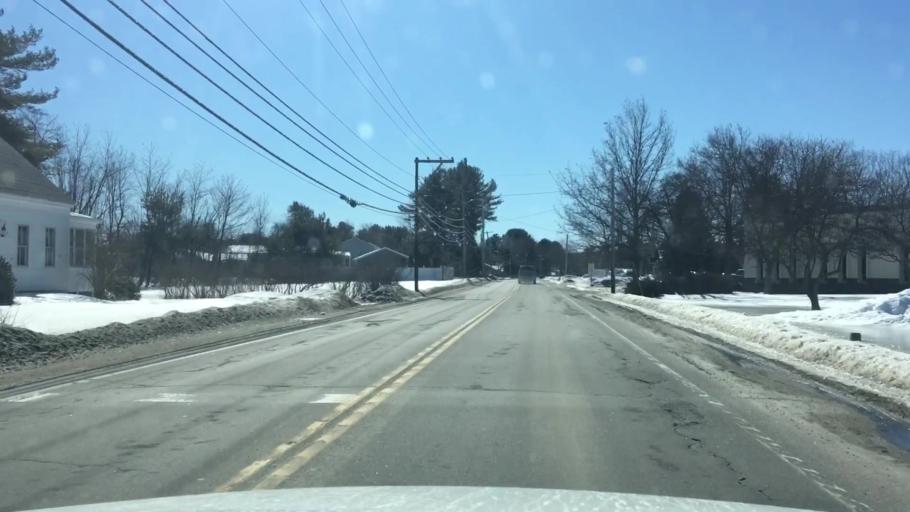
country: US
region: Maine
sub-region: Sagadahoc County
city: Topsham
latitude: 43.9099
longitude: -69.9897
